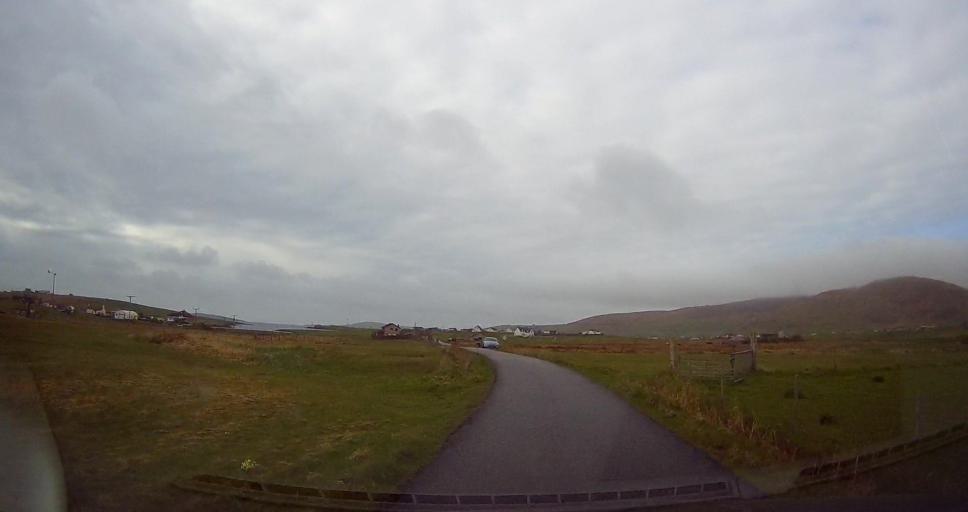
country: GB
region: Scotland
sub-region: Shetland Islands
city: Sandwick
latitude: 60.0470
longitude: -1.2166
